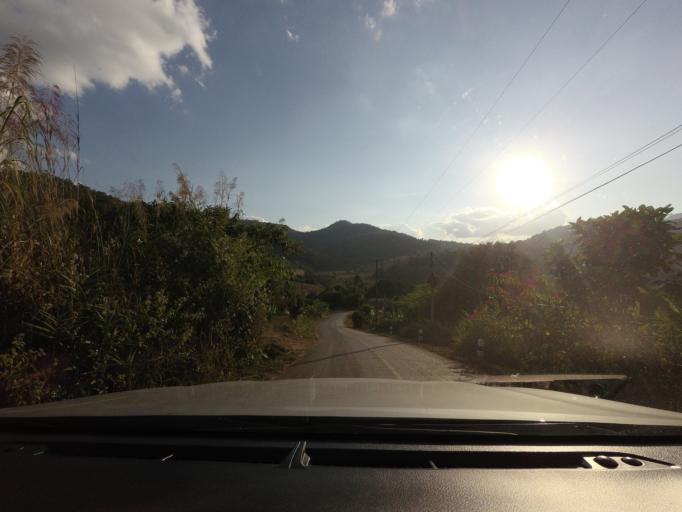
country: TH
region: Chiang Mai
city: Phrao
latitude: 19.4963
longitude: 99.1669
